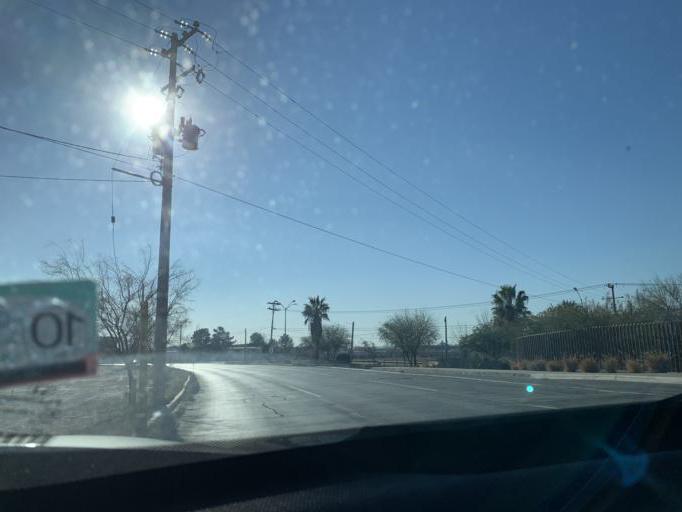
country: US
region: Texas
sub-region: El Paso County
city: Socorro
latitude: 31.6844
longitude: -106.3967
